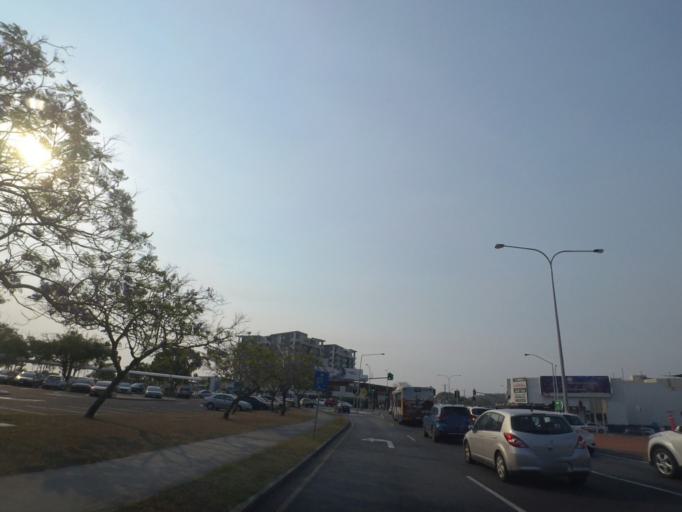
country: AU
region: Queensland
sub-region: Brisbane
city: Upper Mount Gravatt
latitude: -27.5605
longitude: 153.0817
